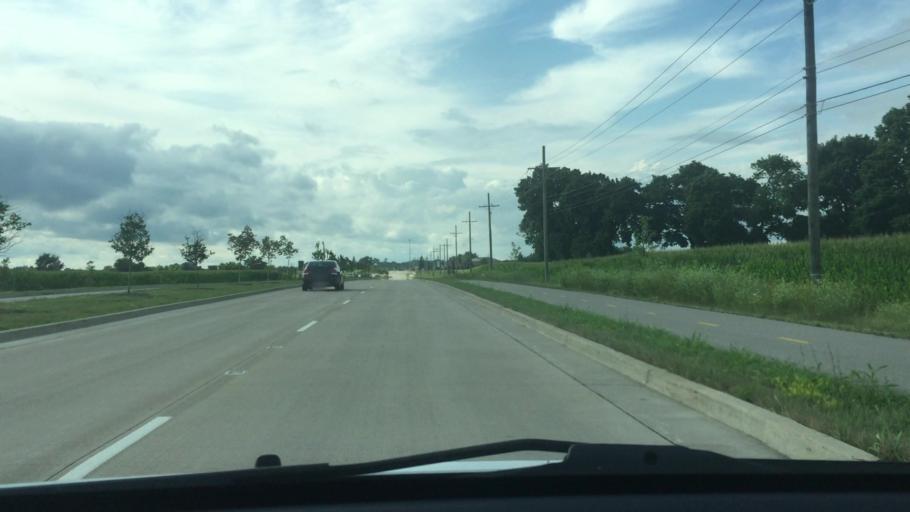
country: US
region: Illinois
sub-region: McHenry County
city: Lakewood
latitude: 42.2619
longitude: -88.3737
